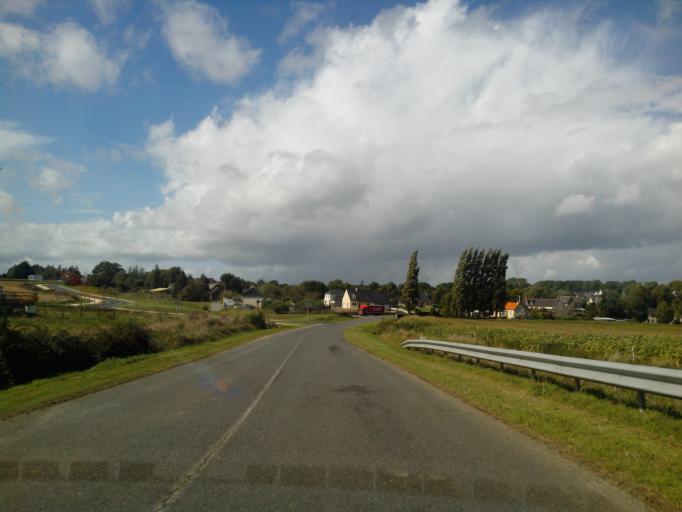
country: FR
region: Brittany
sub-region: Departement des Cotes-d'Armor
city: Merdrignac
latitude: 48.1862
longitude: -2.4146
